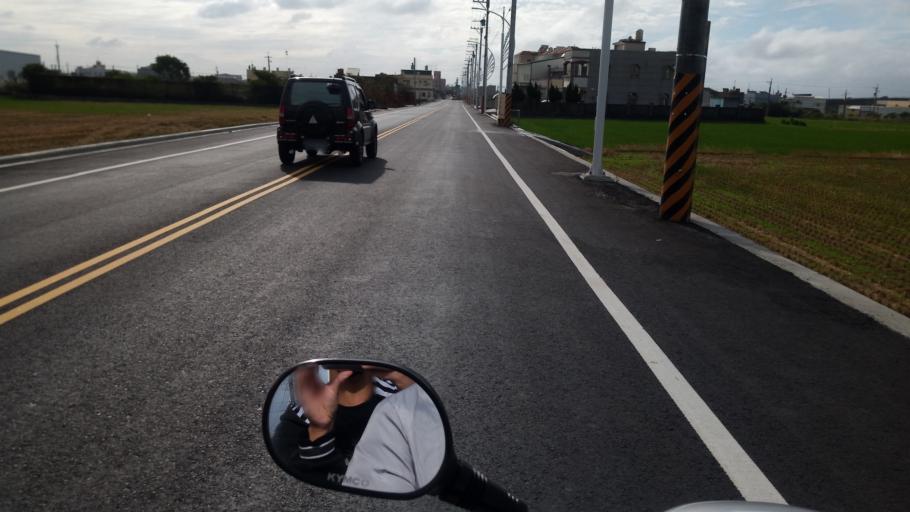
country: TW
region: Taiwan
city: Fengyuan
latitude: 24.4211
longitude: 120.6586
